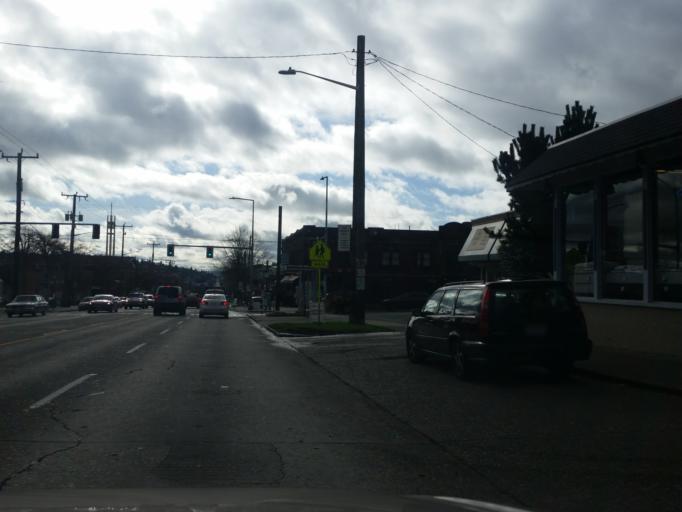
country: US
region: Washington
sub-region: King County
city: Seattle
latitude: 47.6729
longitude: -122.3763
